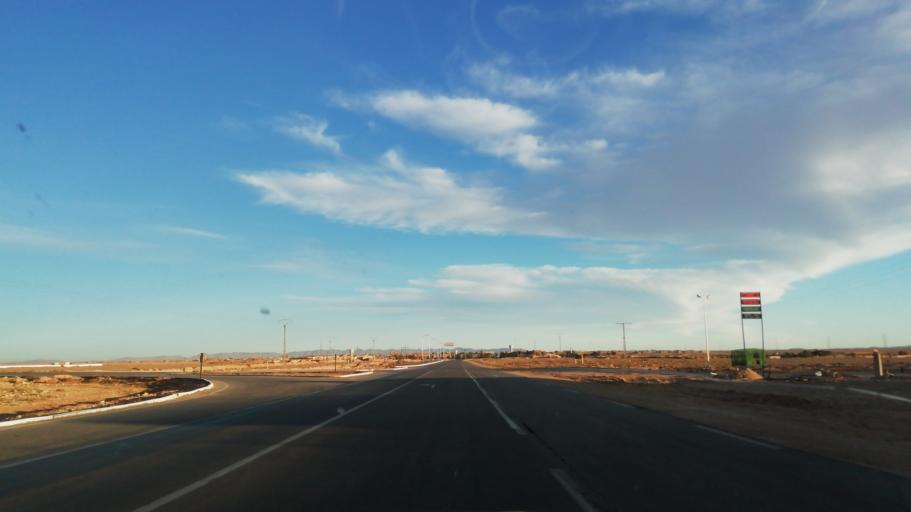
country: DZ
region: Wilaya de Naama
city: Naama
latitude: 33.7260
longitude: -0.7436
